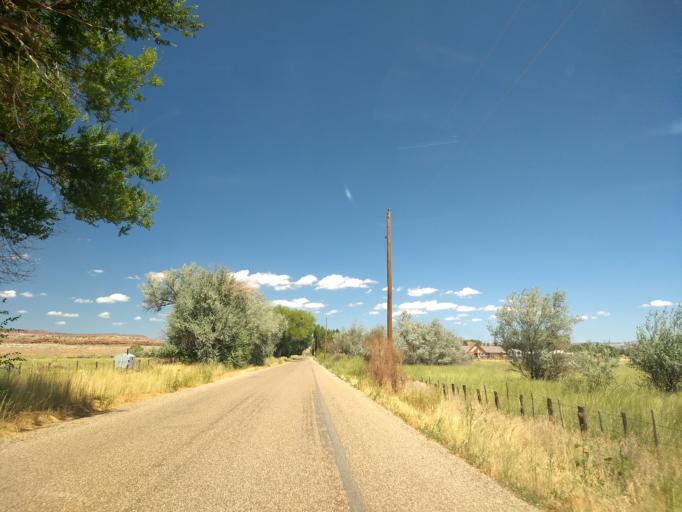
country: US
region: Arizona
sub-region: Coconino County
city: Fredonia
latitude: 36.9387
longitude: -112.5353
